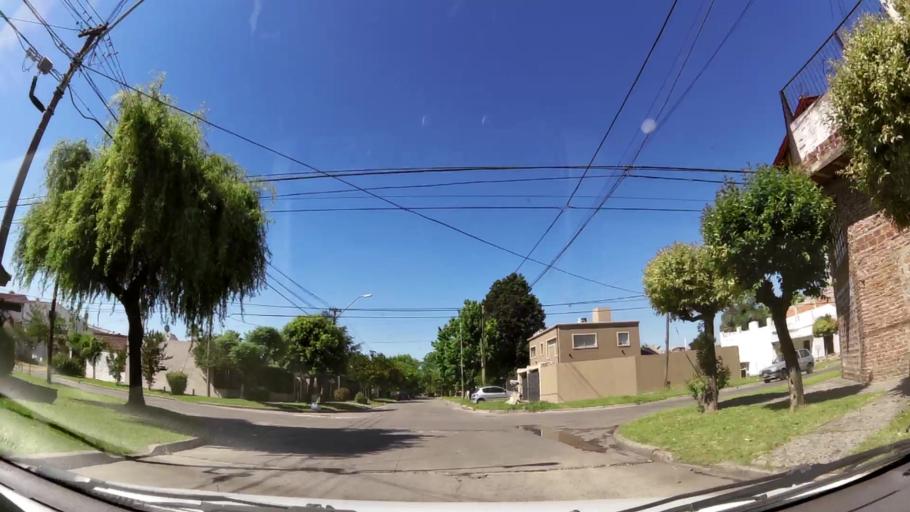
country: AR
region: Buenos Aires
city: Ituzaingo
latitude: -34.6410
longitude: -58.6610
